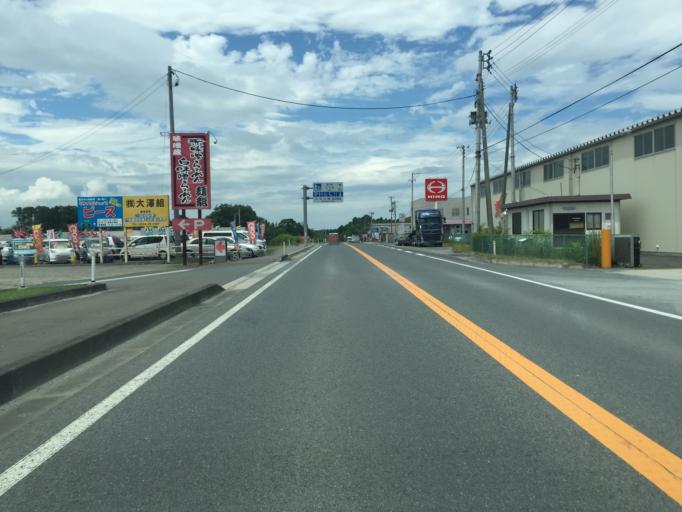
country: JP
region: Miyagi
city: Marumori
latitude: 37.7453
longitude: 140.9543
